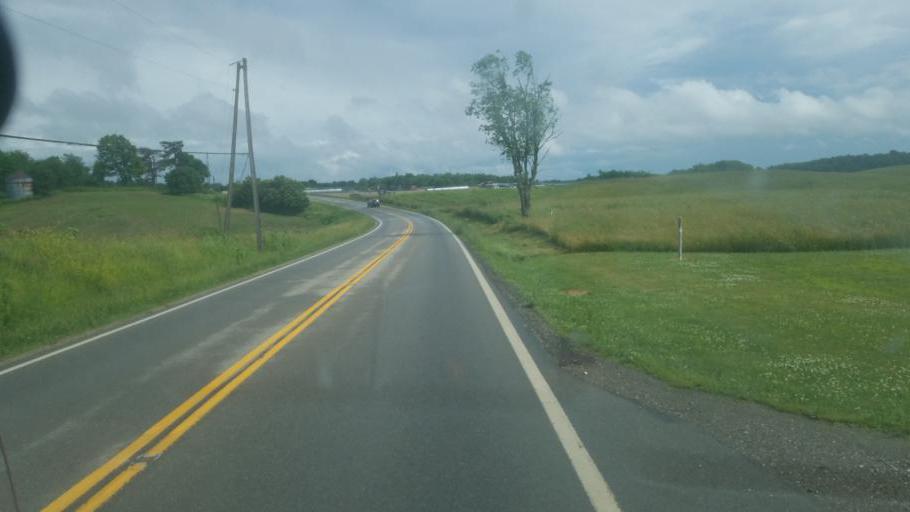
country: US
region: Ohio
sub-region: Carroll County
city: Carrollton
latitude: 40.4601
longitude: -80.9994
